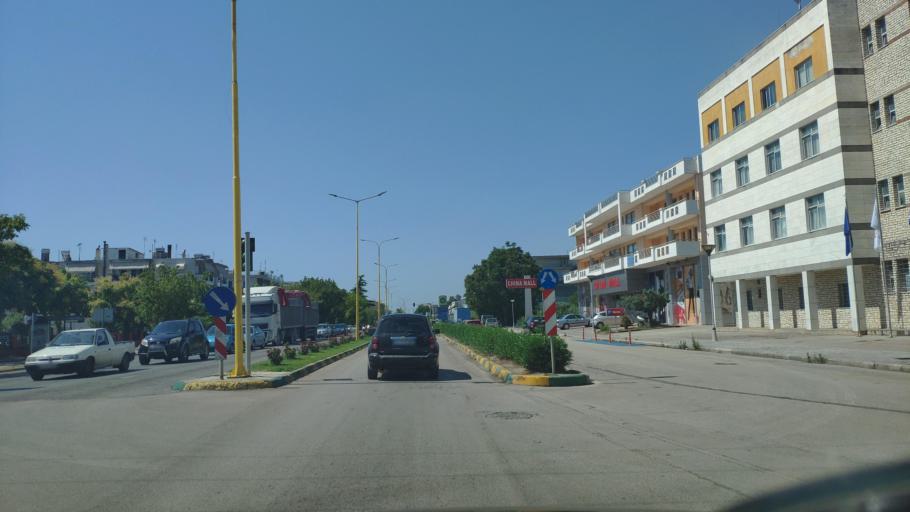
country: GR
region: Epirus
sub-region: Nomos Artas
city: Arta
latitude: 39.1572
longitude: 20.9792
